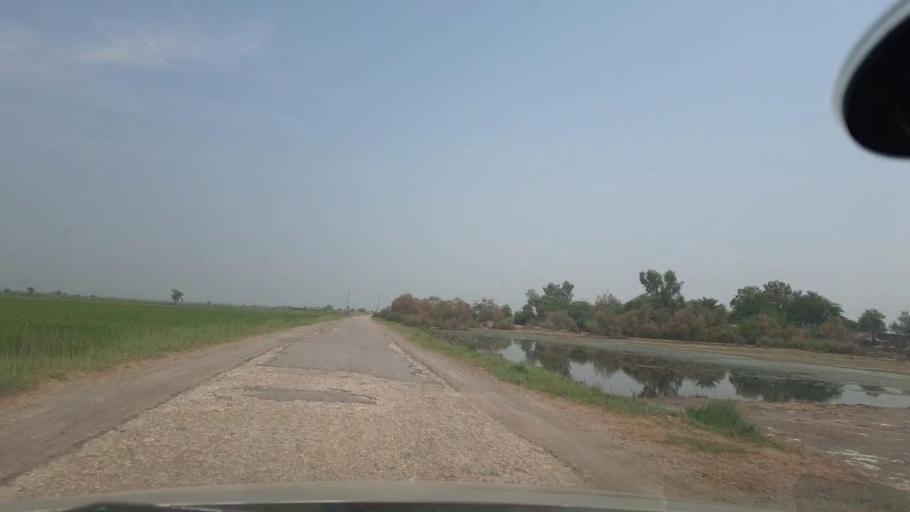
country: PK
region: Sindh
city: Jacobabad
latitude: 28.1412
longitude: 68.3602
